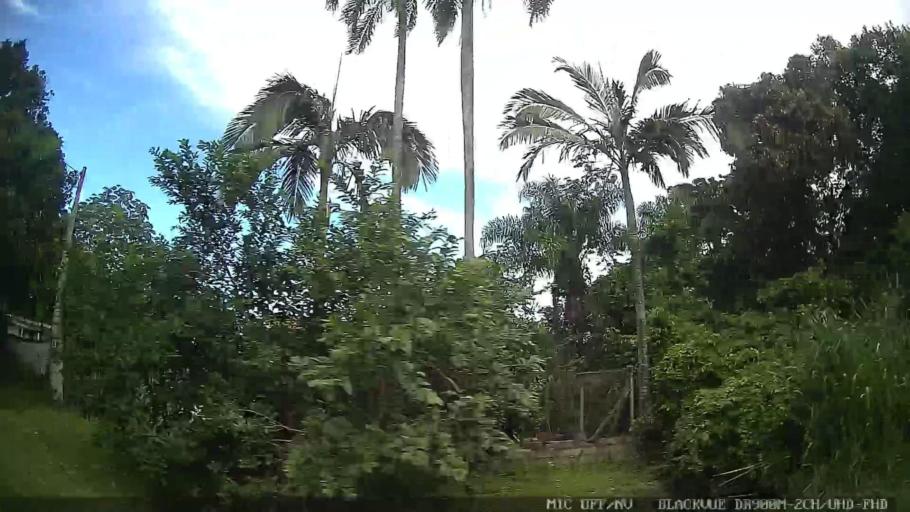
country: BR
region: Sao Paulo
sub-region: Iguape
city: Iguape
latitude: -24.6603
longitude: -47.4151
